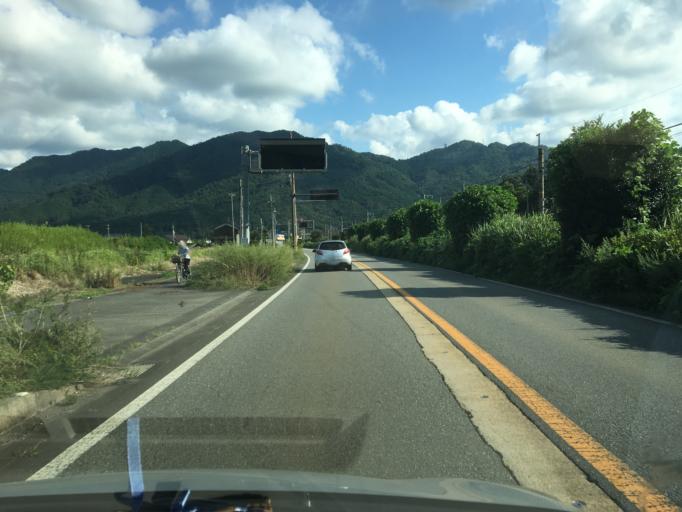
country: JP
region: Hyogo
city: Toyooka
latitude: 35.4272
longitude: 134.7881
